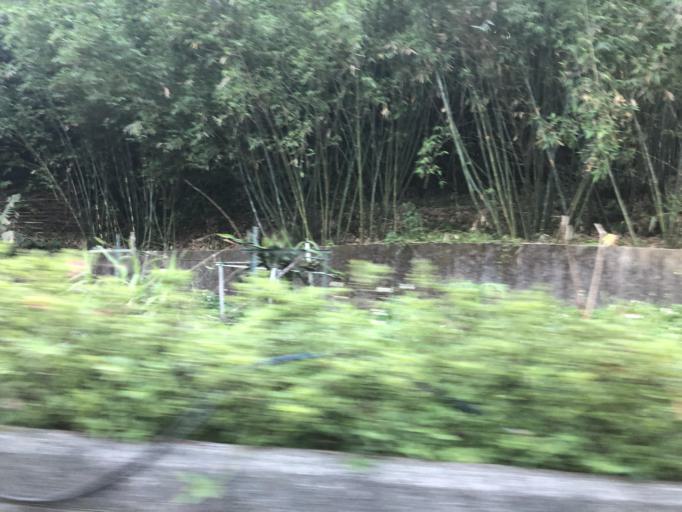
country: TW
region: Taiwan
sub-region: Keelung
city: Keelung
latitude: 25.1983
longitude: 121.6467
